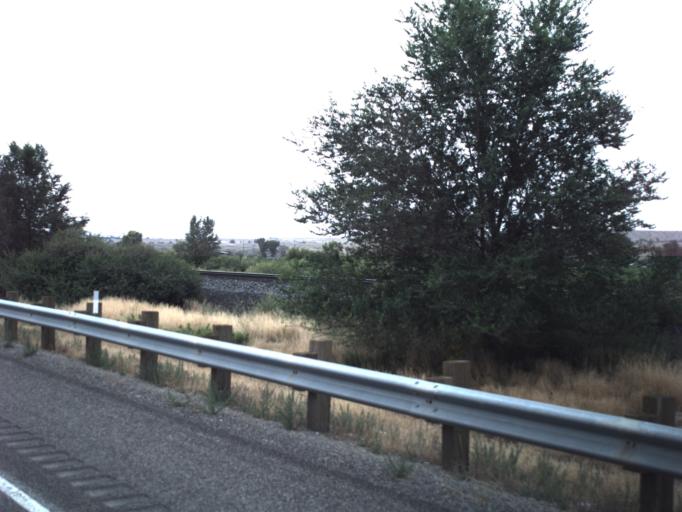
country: US
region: Utah
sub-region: Carbon County
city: Price
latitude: 39.5718
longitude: -110.7819
